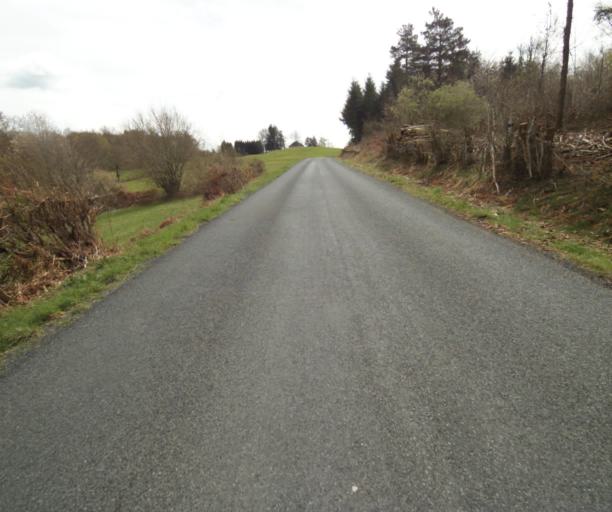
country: FR
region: Limousin
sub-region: Departement de la Correze
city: Sainte-Fortunade
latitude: 45.2008
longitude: 1.8336
